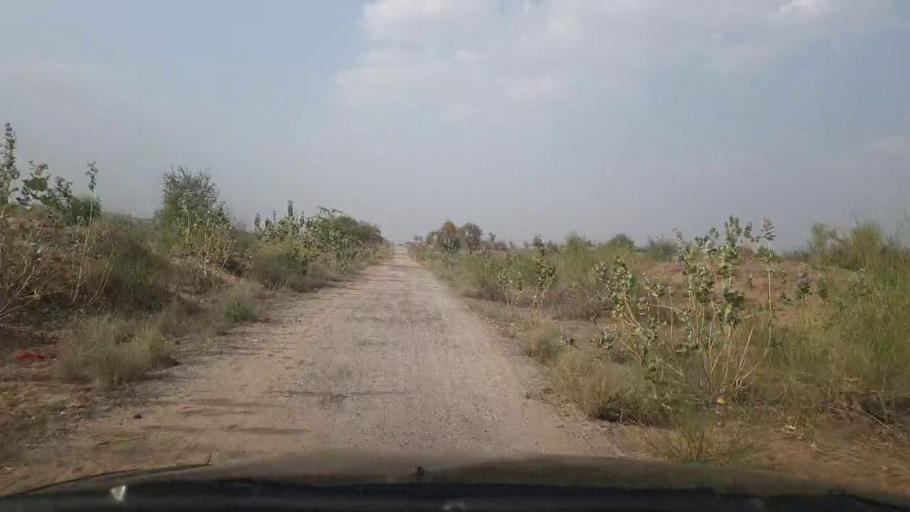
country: PK
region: Sindh
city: Islamkot
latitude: 25.0263
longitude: 70.5597
